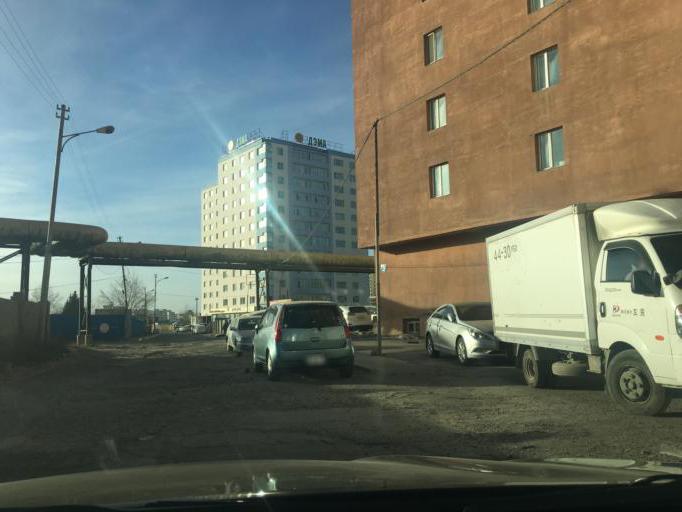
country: MN
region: Ulaanbaatar
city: Ulaanbaatar
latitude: 47.9066
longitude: 106.8934
